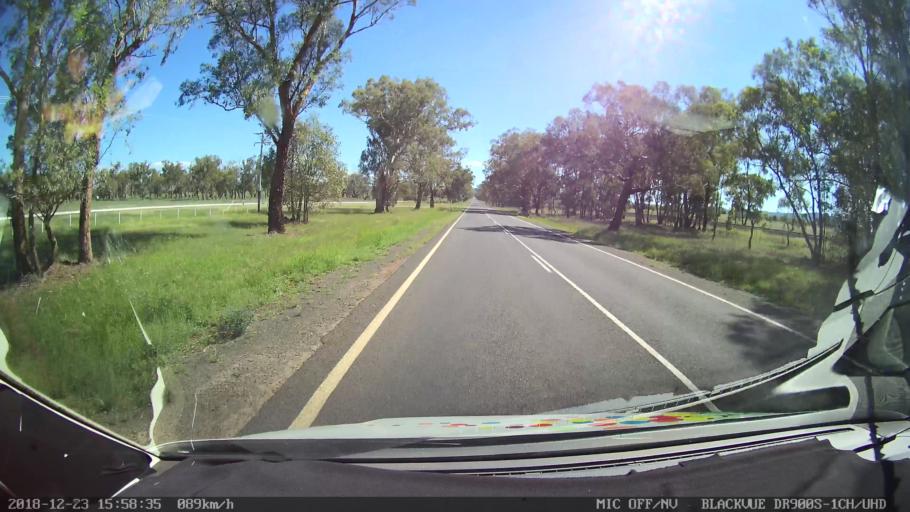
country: AU
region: New South Wales
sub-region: Tamworth Municipality
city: Phillip
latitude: -31.1900
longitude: 150.8404
